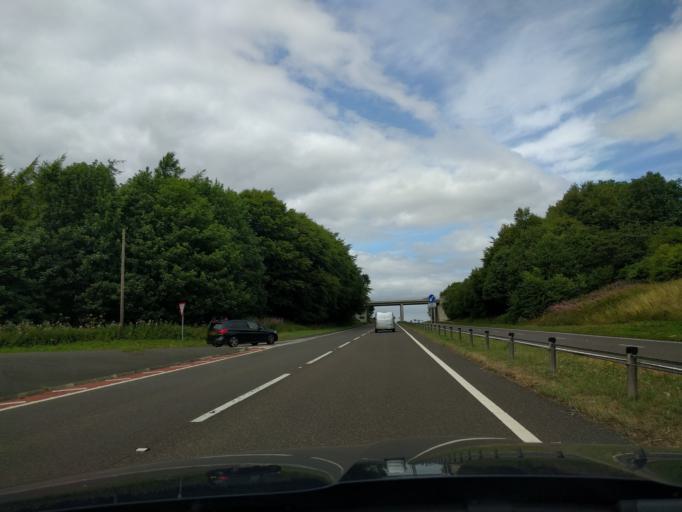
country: GB
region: England
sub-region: Northumberland
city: Alnwick
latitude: 55.4209
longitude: -1.6818
